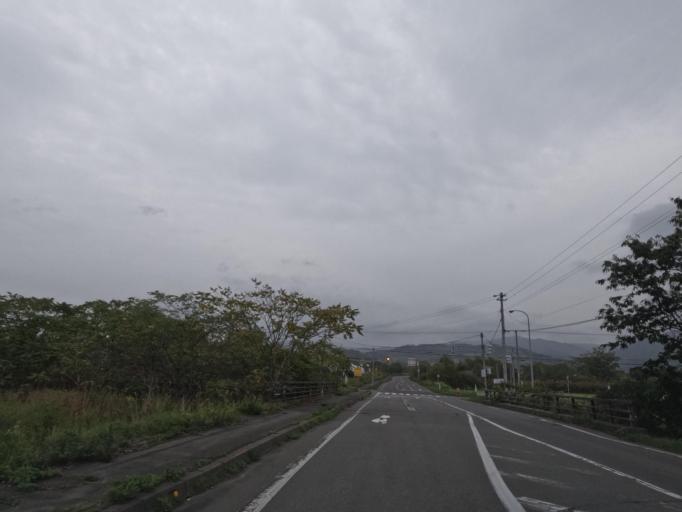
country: JP
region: Hokkaido
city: Date
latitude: 42.5050
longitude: 140.8735
